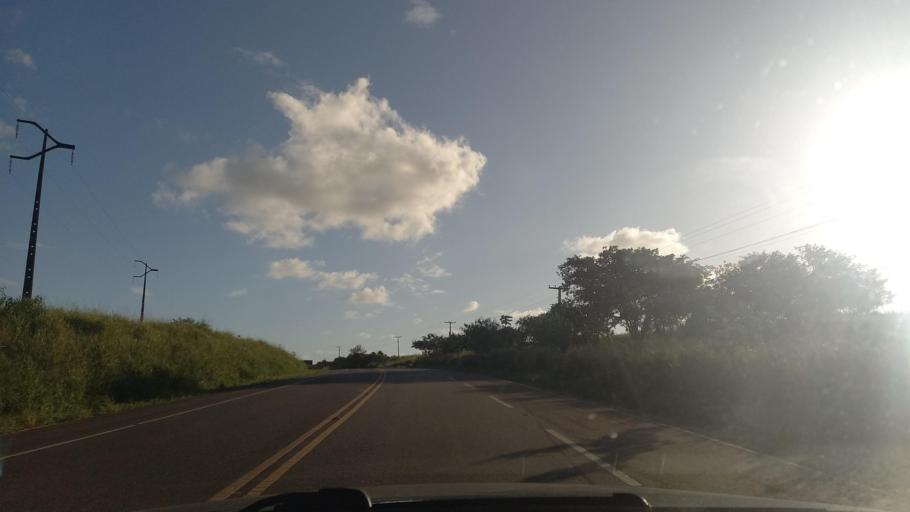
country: BR
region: Alagoas
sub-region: Sao Miguel Dos Campos
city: Sao Miguel dos Campos
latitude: -9.8047
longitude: -36.2054
